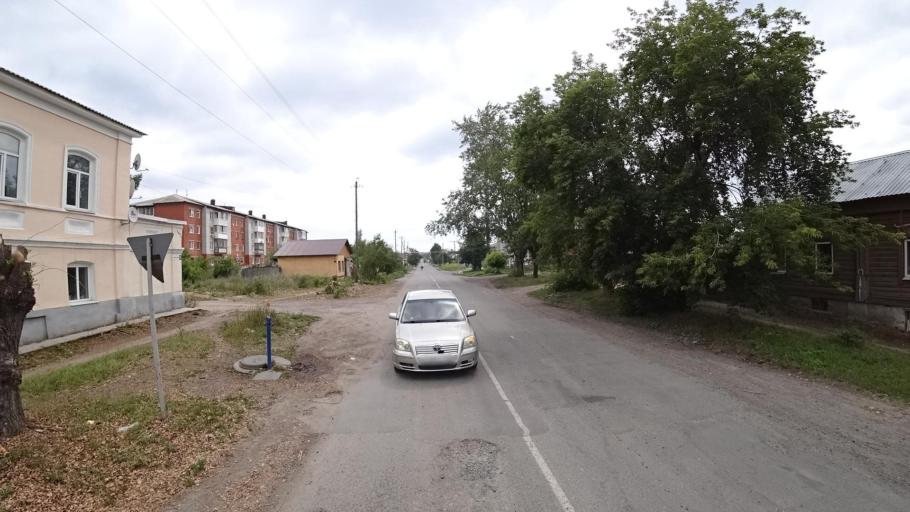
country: RU
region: Sverdlovsk
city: Kamyshlov
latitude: 56.8413
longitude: 62.7052
